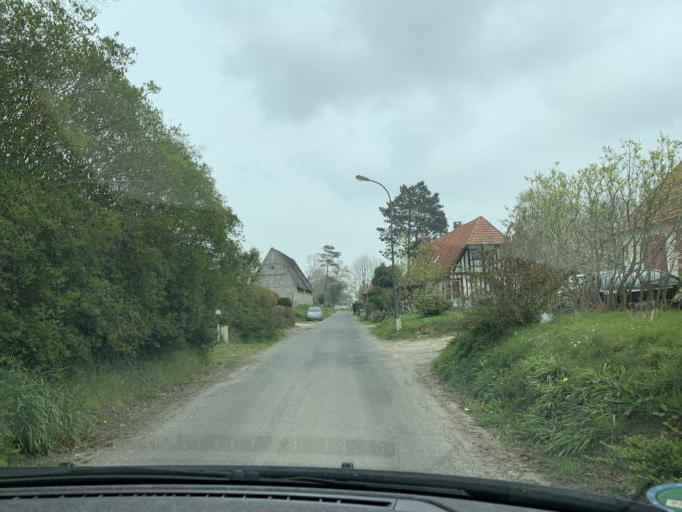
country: FR
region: Haute-Normandie
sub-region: Departement de la Seine-Maritime
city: Fontaine-le-Dun
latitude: 49.8545
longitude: 0.8040
